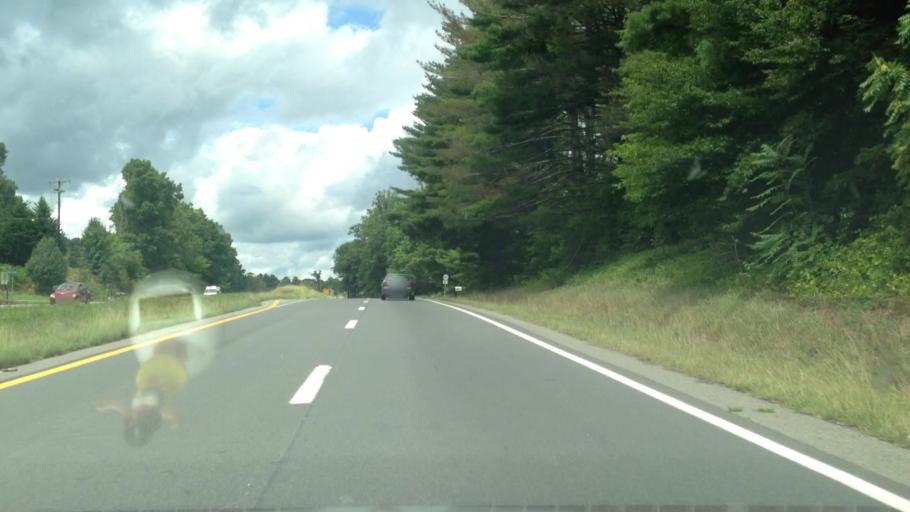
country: US
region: Virginia
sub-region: Henry County
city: Stanleytown
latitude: 36.8038
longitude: -79.9373
